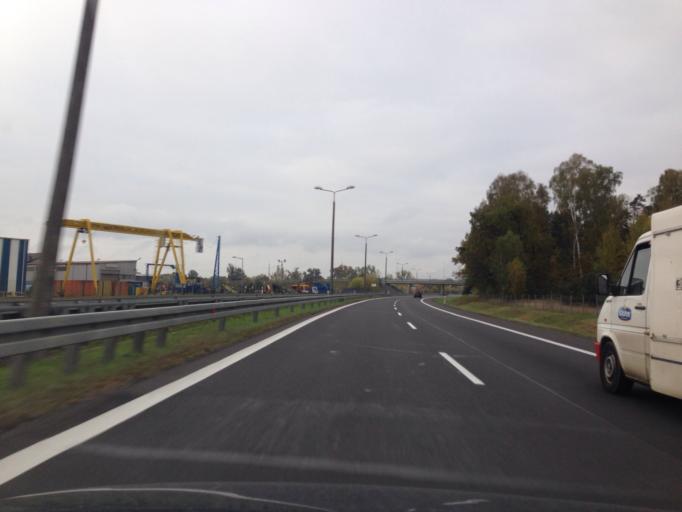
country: PL
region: Kujawsko-Pomorskie
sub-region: Powiat chelminski
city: Chelmno
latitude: 53.3827
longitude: 18.3479
